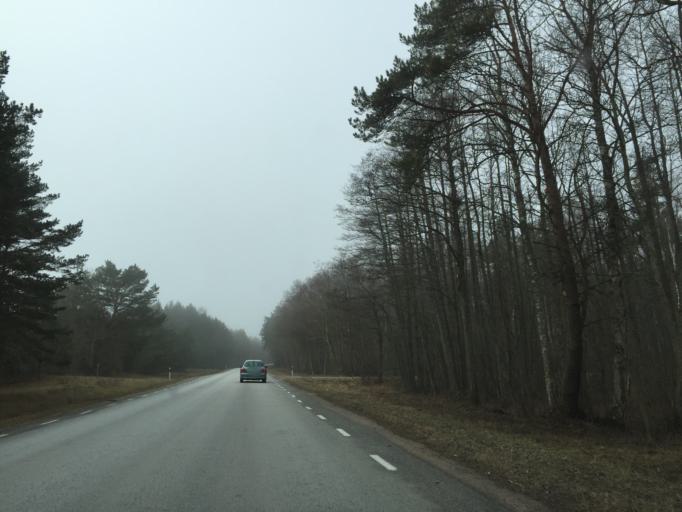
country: EE
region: Saare
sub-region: Kuressaare linn
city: Kuressaare
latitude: 58.2083
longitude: 22.3041
